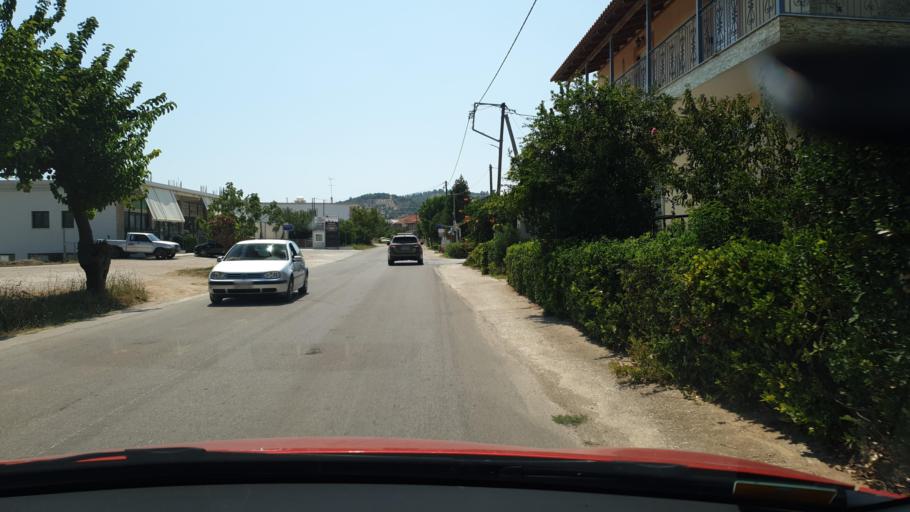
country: GR
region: Central Greece
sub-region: Nomos Evvoias
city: Aliveri
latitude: 38.4532
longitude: 24.1137
